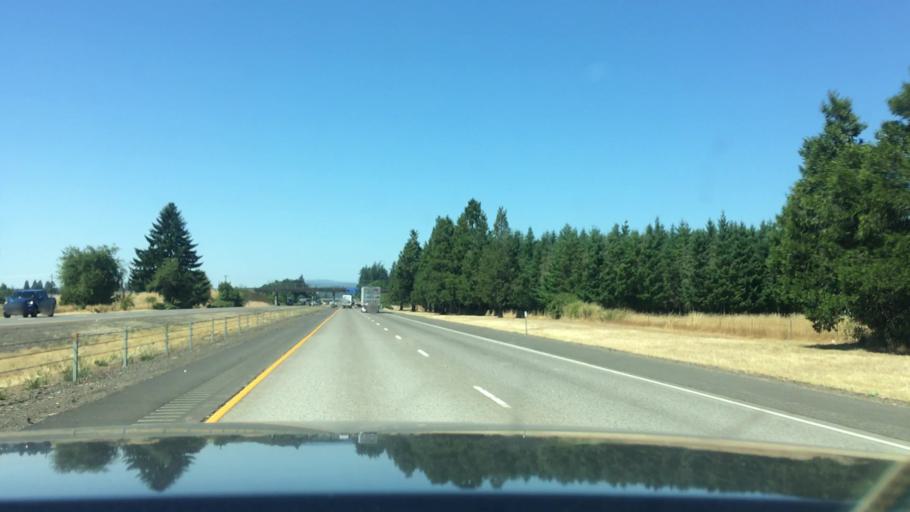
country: US
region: Oregon
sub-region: Lane County
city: Creswell
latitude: 43.9035
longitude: -123.0158
